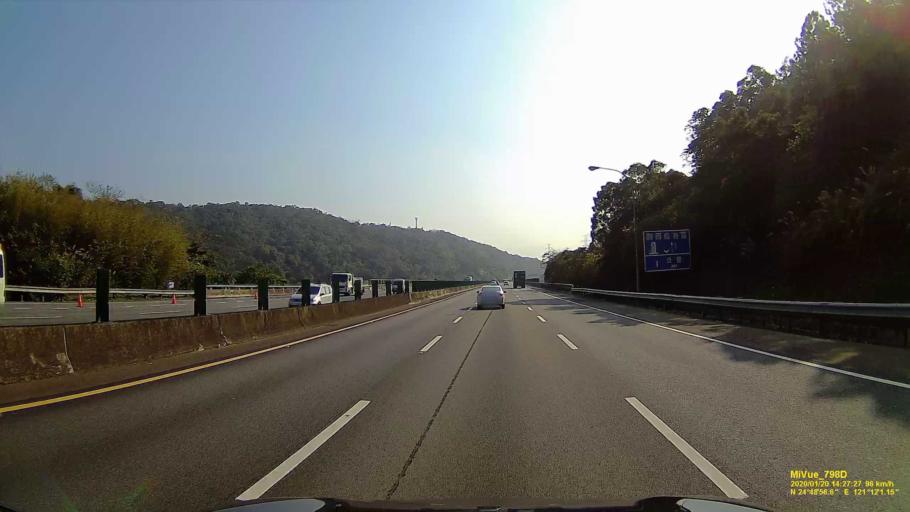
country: TW
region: Taiwan
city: Daxi
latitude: 24.8147
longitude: 121.2002
